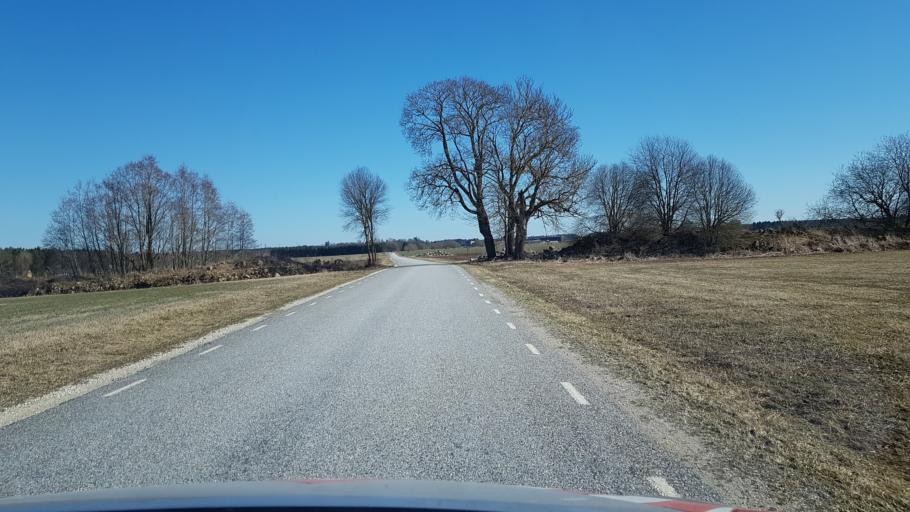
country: EE
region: Laeaene-Virumaa
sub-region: Viru-Nigula vald
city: Kunda
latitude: 59.4025
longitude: 26.5454
